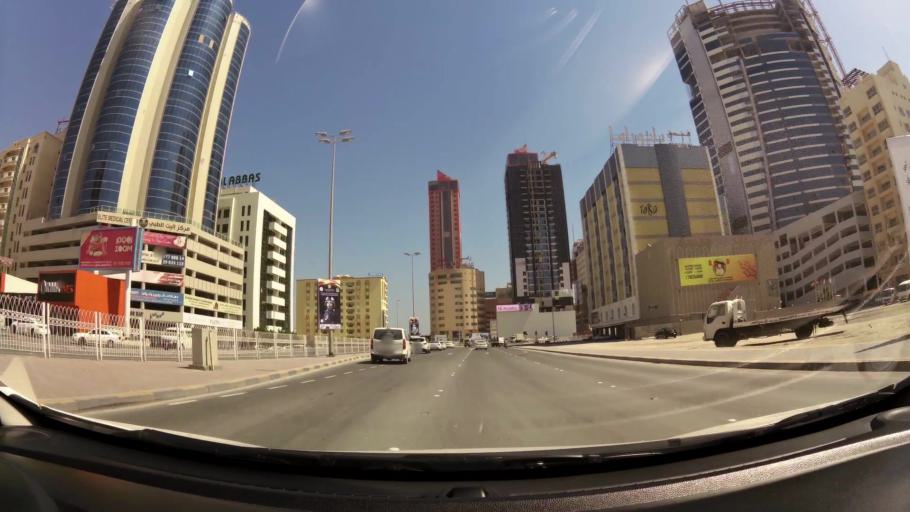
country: BH
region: Manama
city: Manama
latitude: 26.2166
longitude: 50.6084
